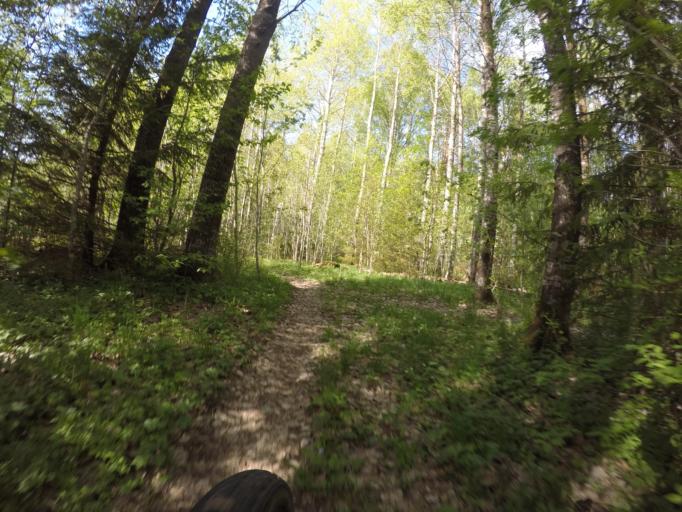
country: SE
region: Vaestmanland
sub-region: Vasteras
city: Vasteras
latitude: 59.6550
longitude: 16.5081
